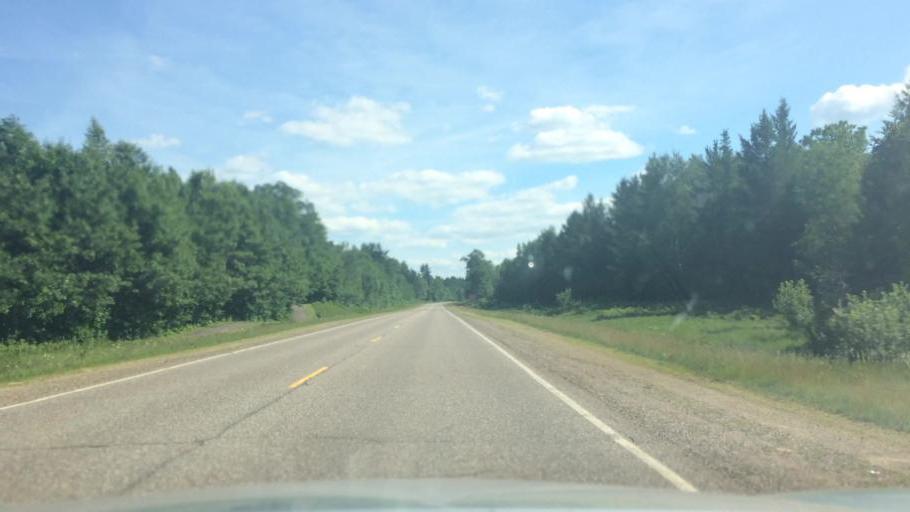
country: US
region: Wisconsin
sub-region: Vilas County
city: Lac du Flambeau
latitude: 46.0804
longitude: -89.6447
